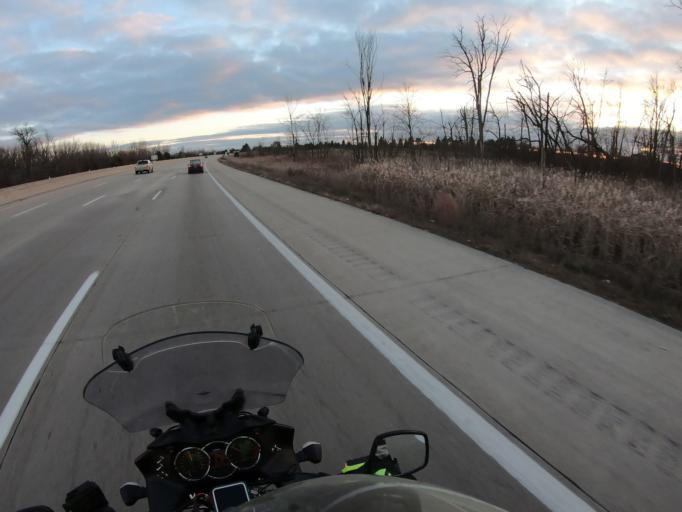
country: US
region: Michigan
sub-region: Saginaw County
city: Birch Run
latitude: 43.2440
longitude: -83.7709
